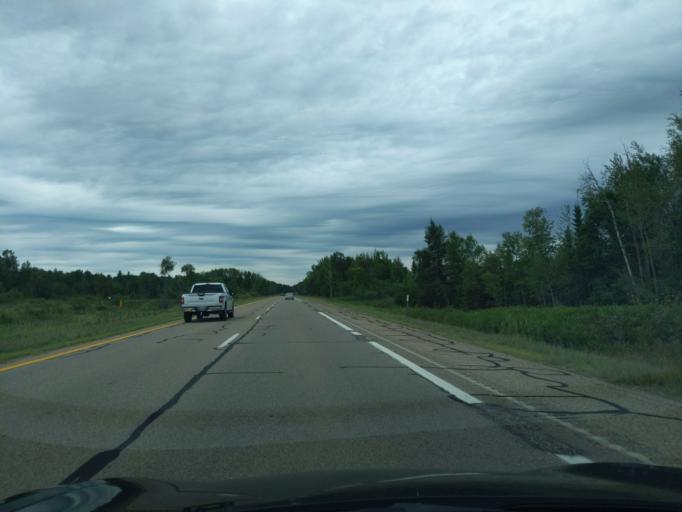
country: US
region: Michigan
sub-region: Roscommon County
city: Houghton Lake
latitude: 44.2879
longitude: -84.8009
